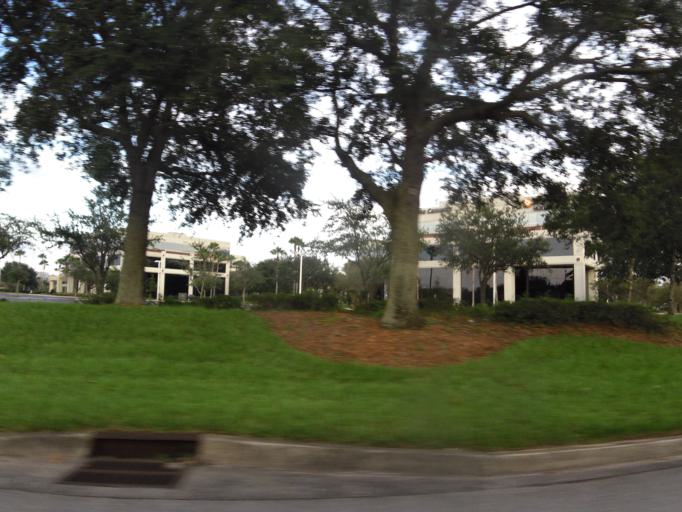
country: US
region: Florida
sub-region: Duval County
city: Jacksonville
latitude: 30.2464
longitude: -81.5358
